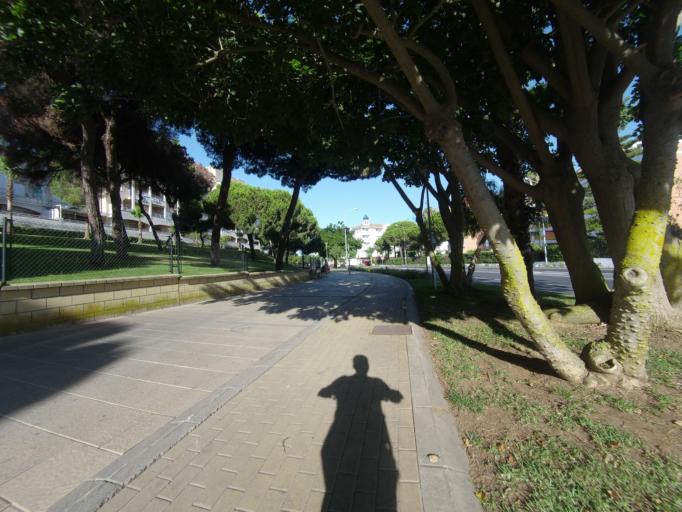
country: ES
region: Andalusia
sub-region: Provincia de Huelva
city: Aljaraque
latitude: 37.2116
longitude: -7.0490
